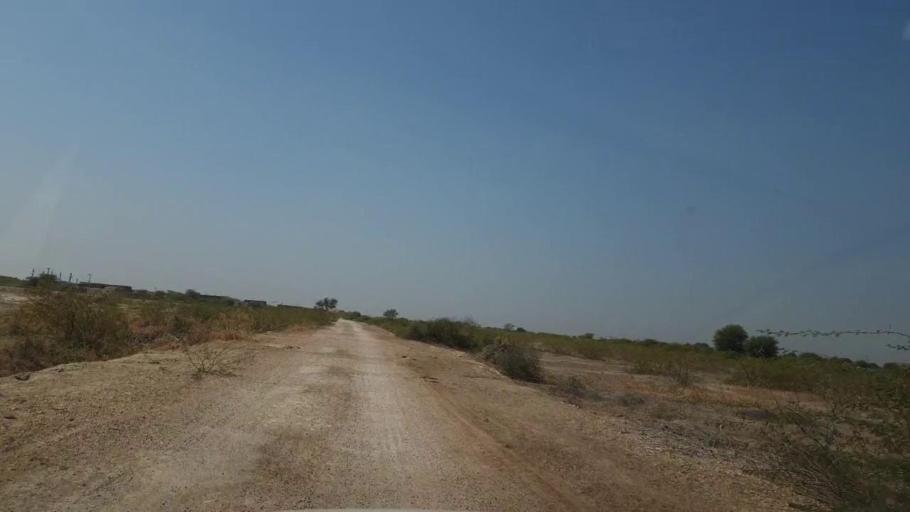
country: PK
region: Sindh
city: Kunri
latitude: 25.0907
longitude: 69.4739
